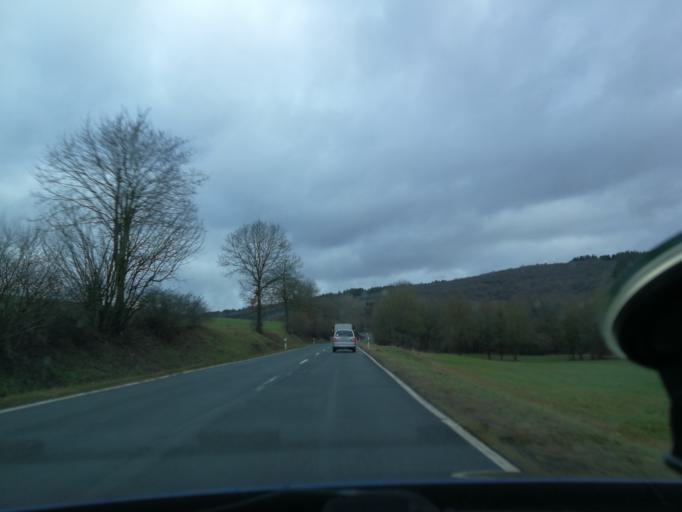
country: DE
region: Rheinland-Pfalz
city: Oberehe-Stroheich
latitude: 50.2707
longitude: 6.7728
